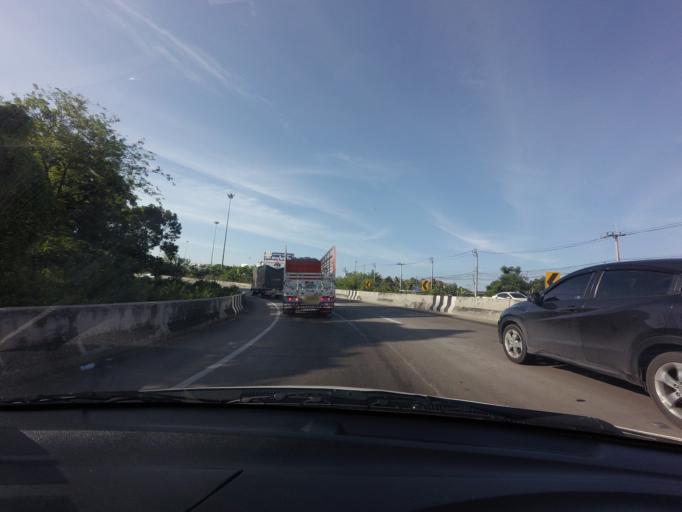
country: TH
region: Nonthaburi
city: Bang Bua Thong
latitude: 13.8728
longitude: 100.4085
